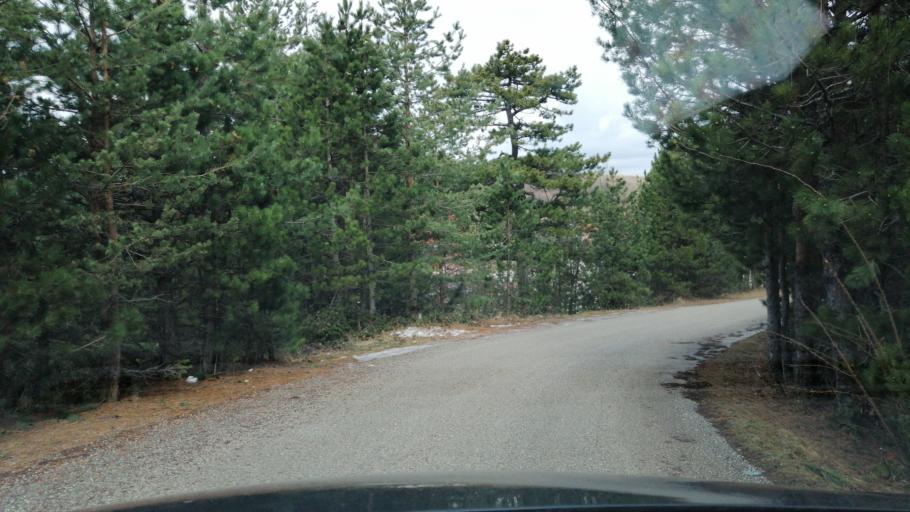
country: RS
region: Central Serbia
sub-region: Zlatiborski Okrug
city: Bajina Basta
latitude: 43.8923
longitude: 19.5558
